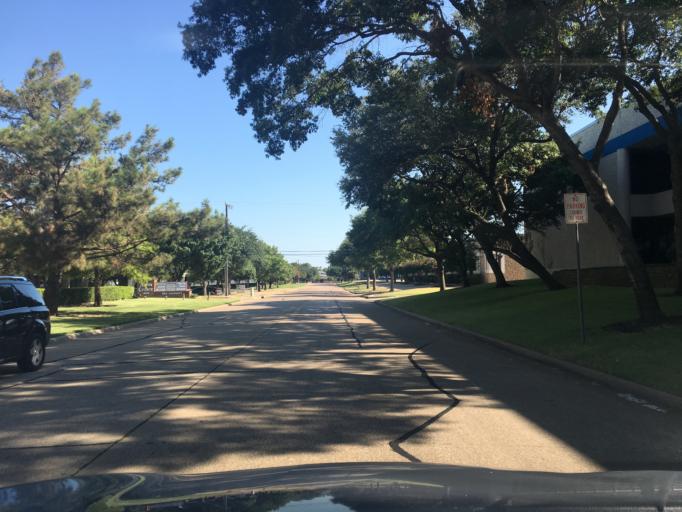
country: US
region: Texas
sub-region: Dallas County
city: Addison
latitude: 32.9653
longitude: -96.8449
